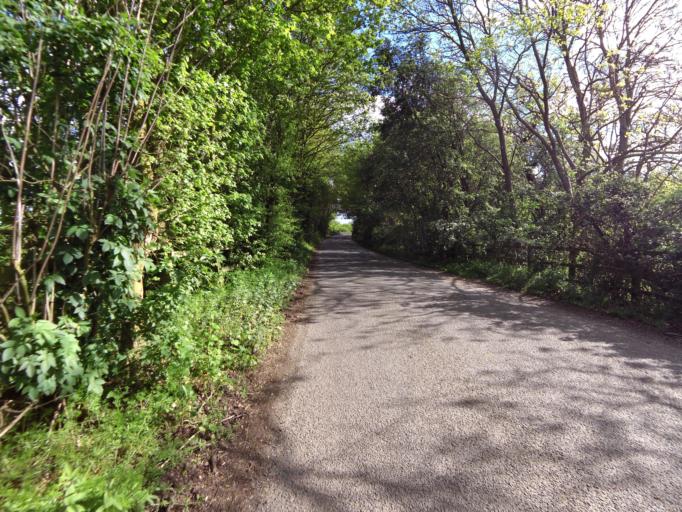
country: GB
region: England
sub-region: Suffolk
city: Woolpit
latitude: 52.2307
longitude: 0.8583
